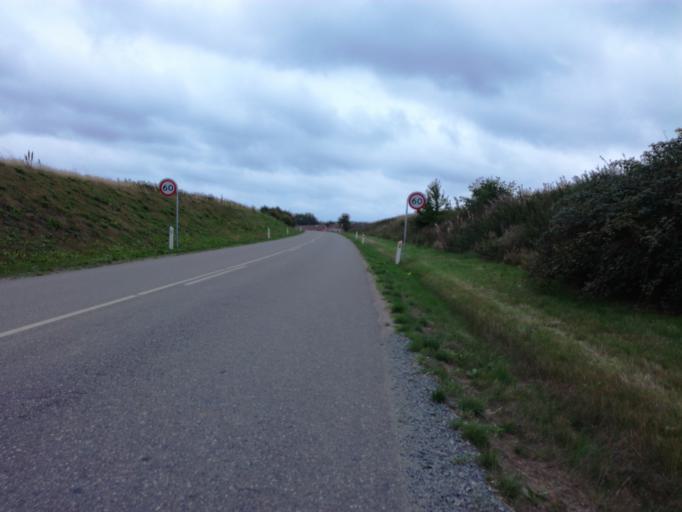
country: DK
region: South Denmark
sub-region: Vejle Kommune
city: Borkop
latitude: 55.6423
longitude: 9.6362
